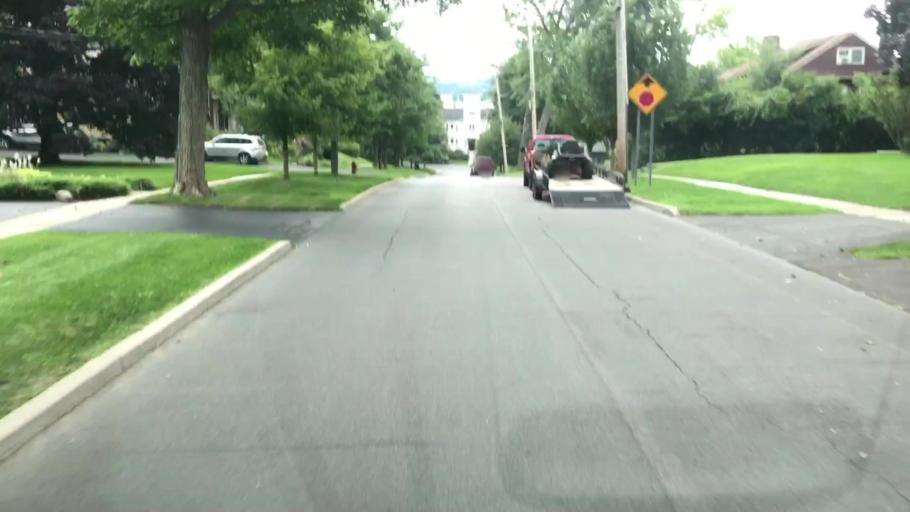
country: US
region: New York
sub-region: Onondaga County
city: Skaneateles
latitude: 42.9469
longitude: -76.4236
